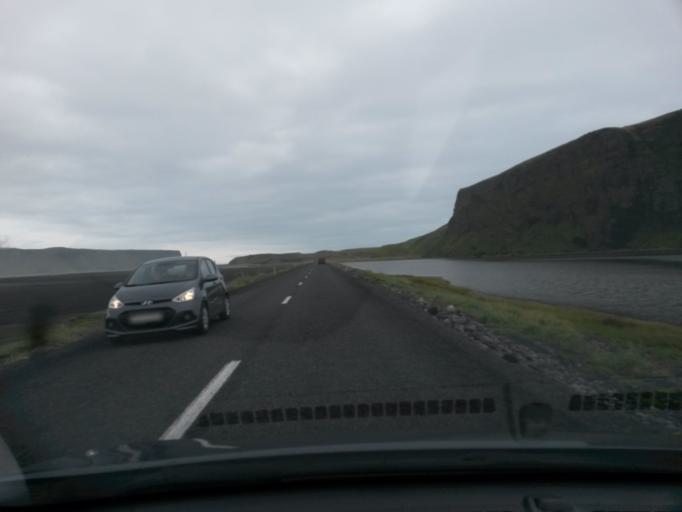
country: IS
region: South
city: Vestmannaeyjar
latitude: 63.4126
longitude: -19.1349
